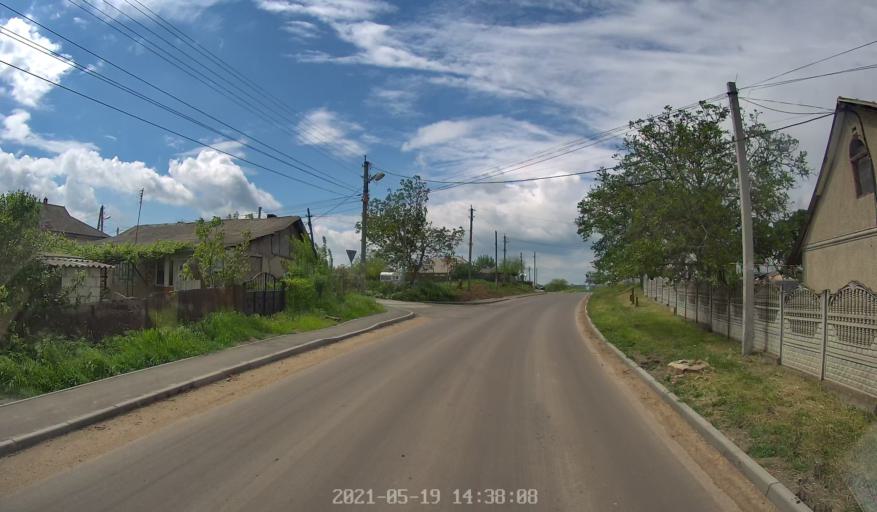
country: MD
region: Chisinau
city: Stauceni
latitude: 47.0444
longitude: 28.9621
